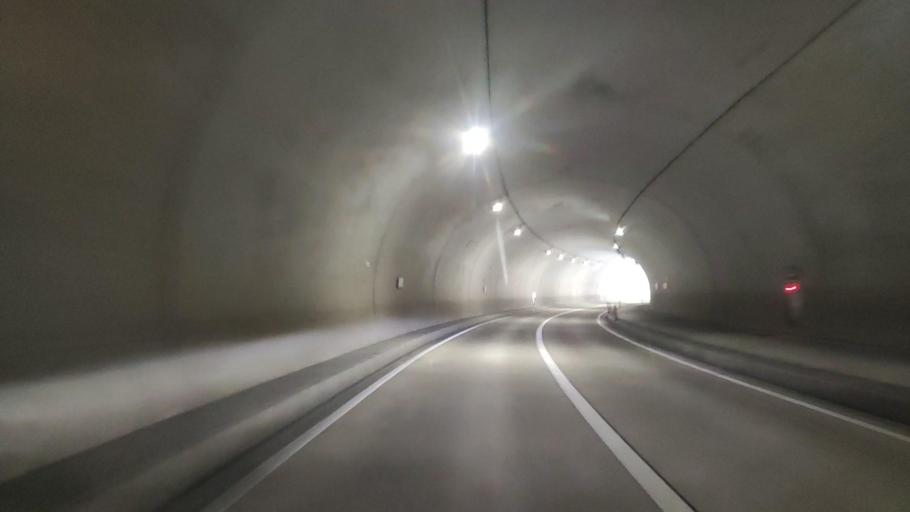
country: JP
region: Shiga Prefecture
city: Nagahama
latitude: 35.3835
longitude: 136.3345
